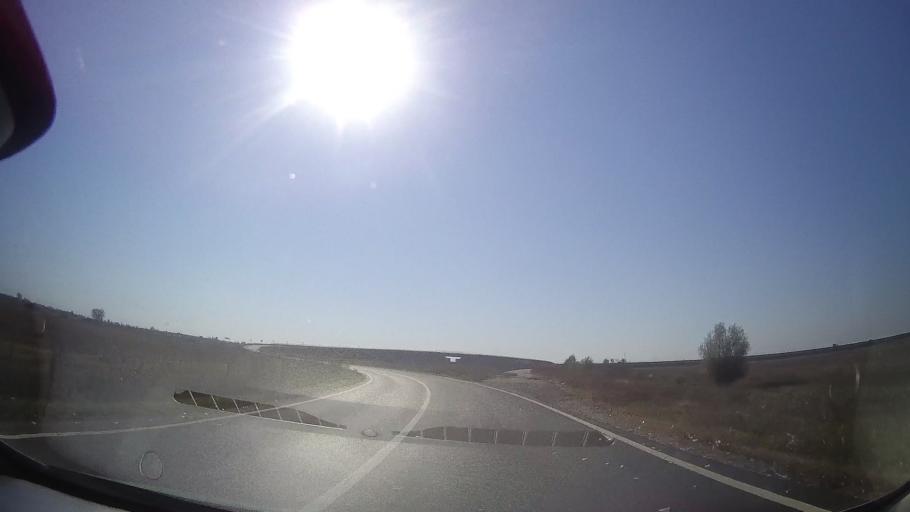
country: RO
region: Timis
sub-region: Comuna Ghizela
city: Ghizela
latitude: 45.7848
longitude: 21.7312
